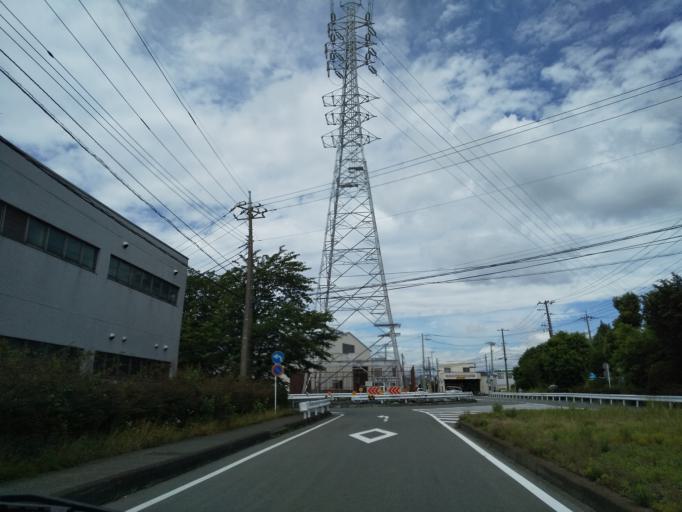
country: JP
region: Kanagawa
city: Zama
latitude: 35.5115
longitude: 139.3423
